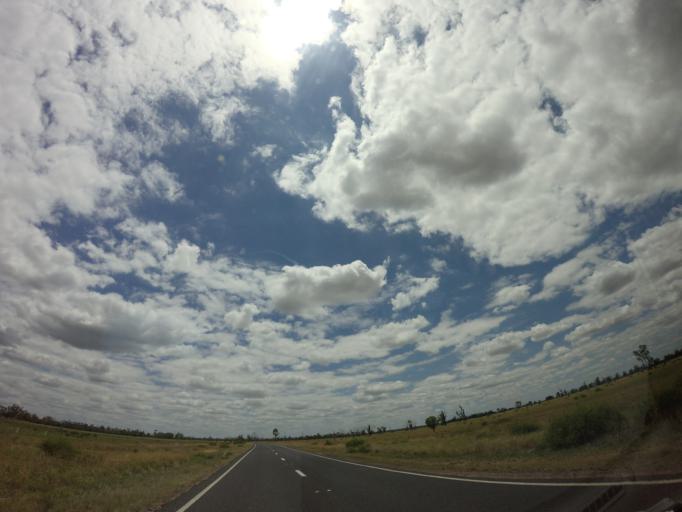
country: AU
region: New South Wales
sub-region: Moree Plains
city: Boggabilla
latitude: -28.6513
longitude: 150.3380
